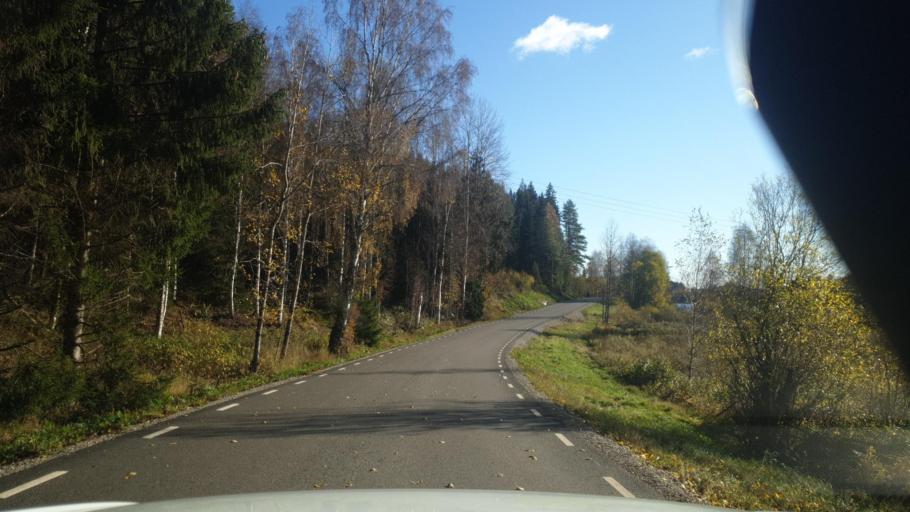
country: SE
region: Vaermland
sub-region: Arvika Kommun
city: Arvika
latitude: 59.6611
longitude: 12.7982
